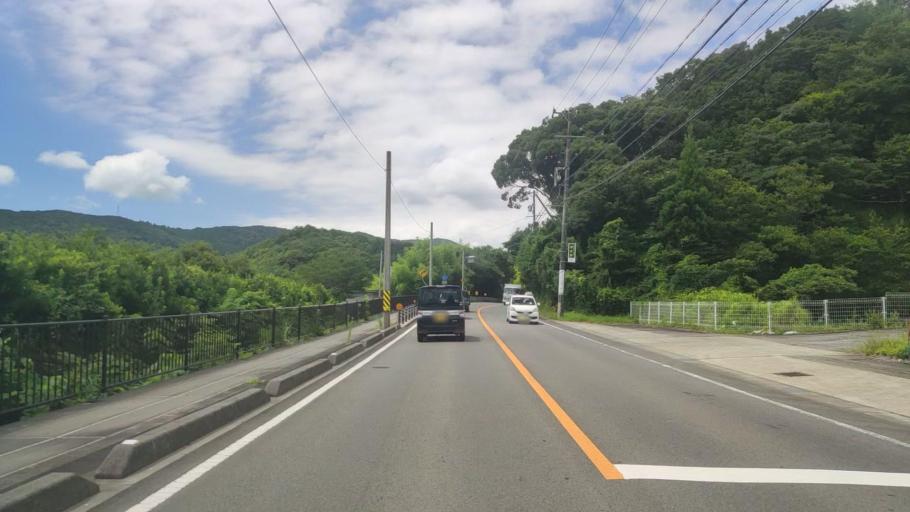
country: JP
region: Mie
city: Toba
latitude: 34.4330
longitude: 136.8394
